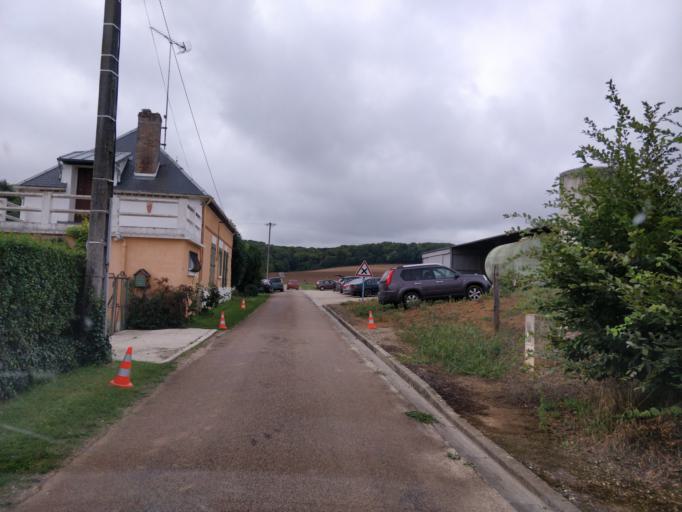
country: FR
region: Bourgogne
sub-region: Departement de l'Yonne
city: Neuvy-Sautour
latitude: 48.1176
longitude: 3.8387
